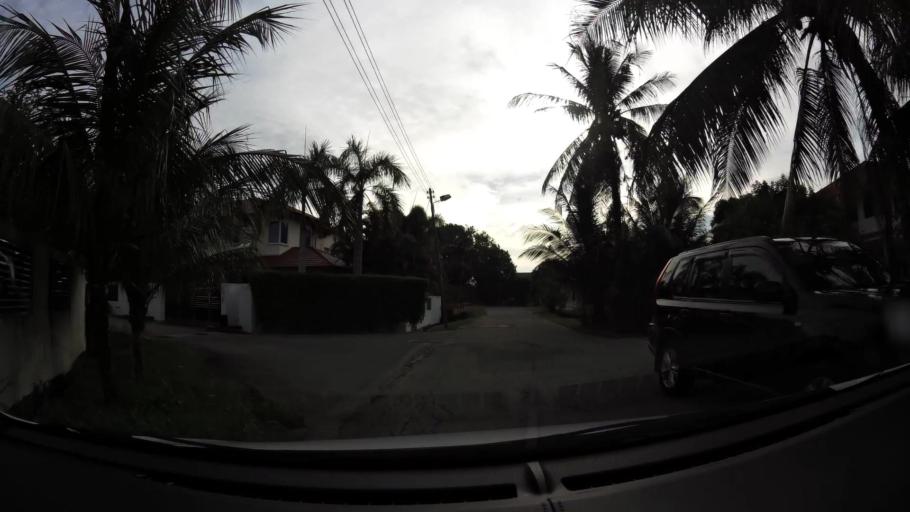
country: BN
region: Brunei and Muara
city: Bandar Seri Begawan
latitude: 4.9025
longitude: 114.8950
